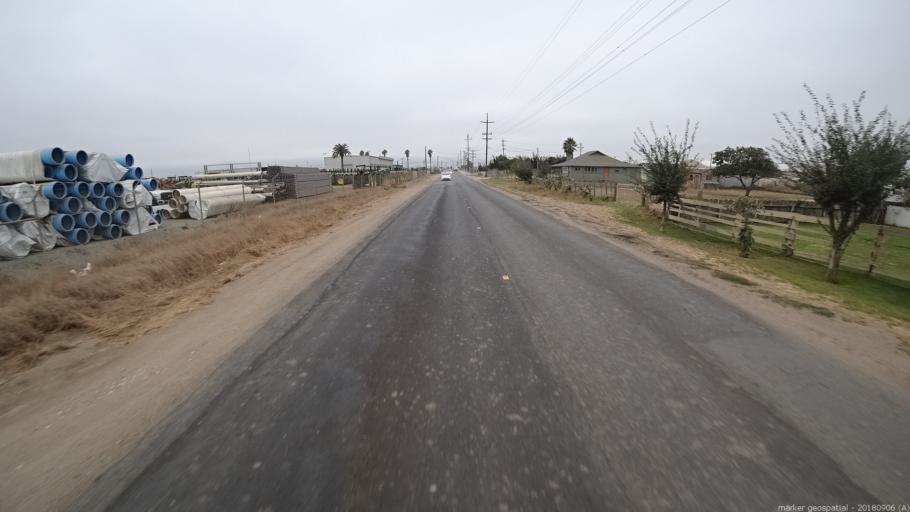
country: US
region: California
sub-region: Monterey County
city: Chualar
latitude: 36.6142
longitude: -121.5644
